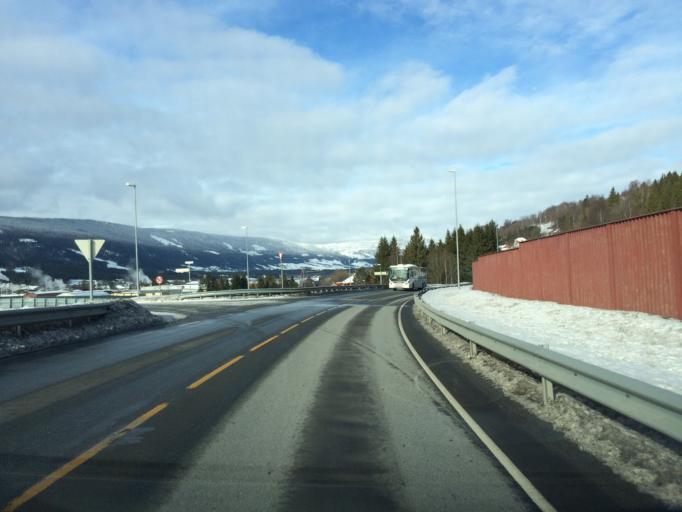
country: NO
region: Oppland
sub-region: Gausdal
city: Segalstad bru
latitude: 61.2233
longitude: 10.2338
